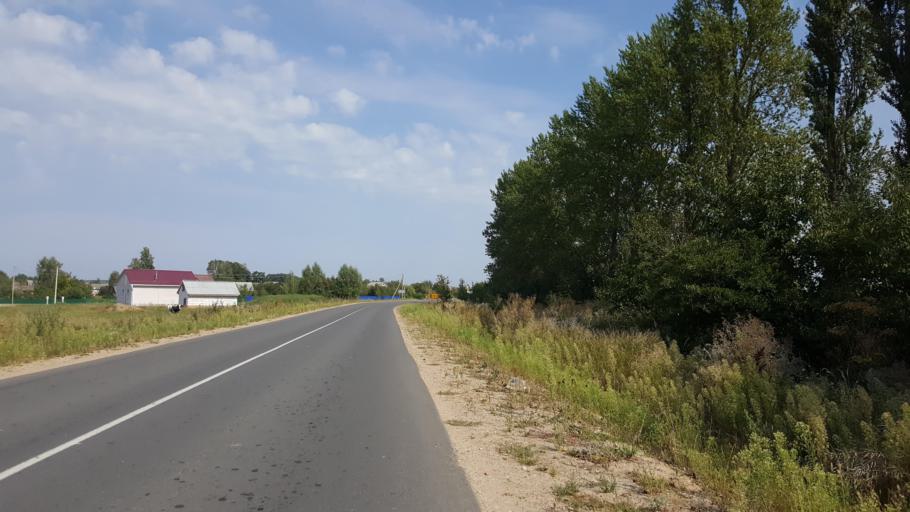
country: BY
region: Brest
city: Kamyanyets
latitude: 52.4619
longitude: 23.7346
